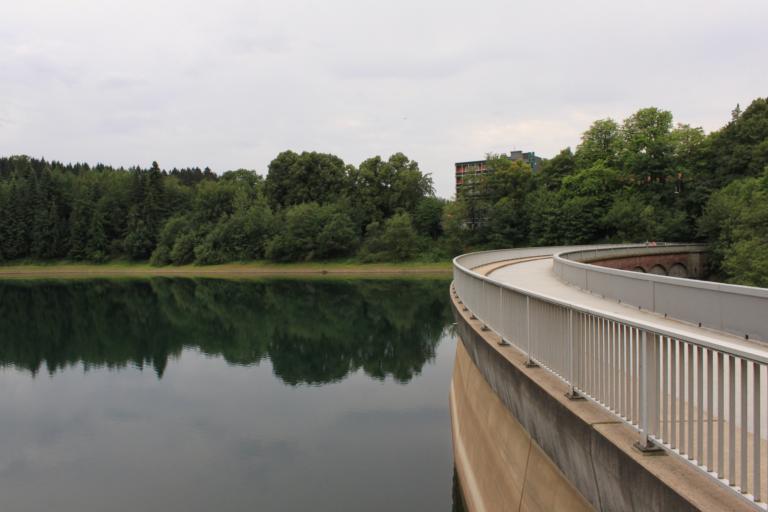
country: DE
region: North Rhine-Westphalia
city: Wermelskirchen
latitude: 51.1601
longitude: 7.2322
